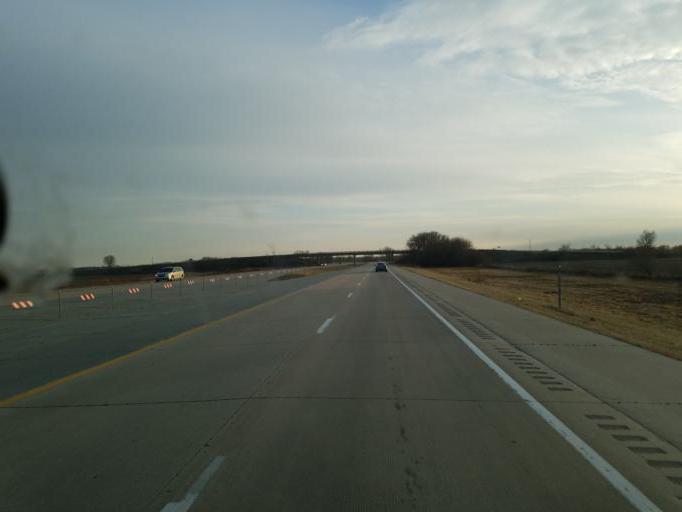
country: US
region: Nebraska
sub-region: Burt County
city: Tekamah
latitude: 41.8601
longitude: -96.1027
